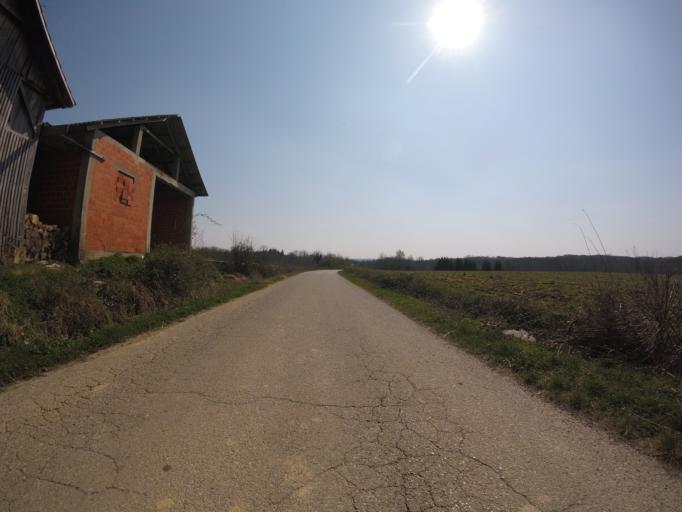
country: HR
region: Grad Zagreb
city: Strmec
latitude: 45.5697
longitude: 15.9217
